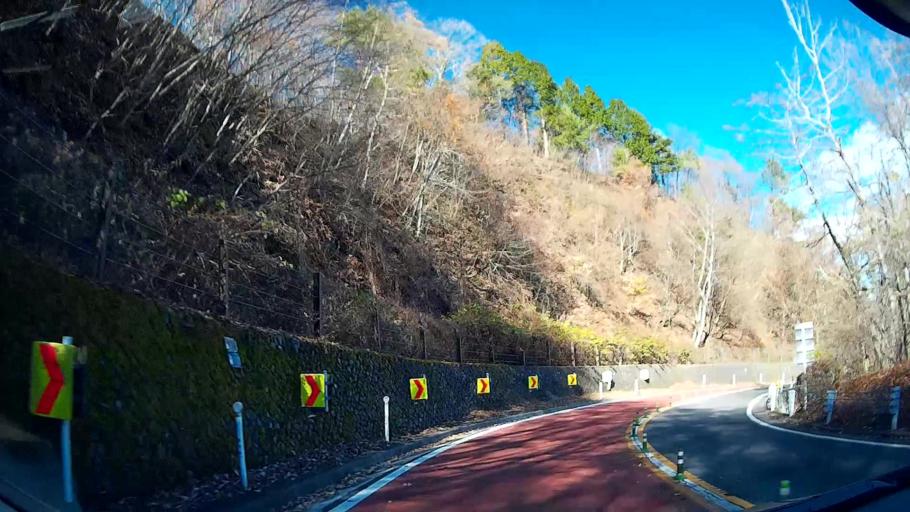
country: JP
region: Yamanashi
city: Uenohara
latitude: 35.7501
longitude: 139.0400
